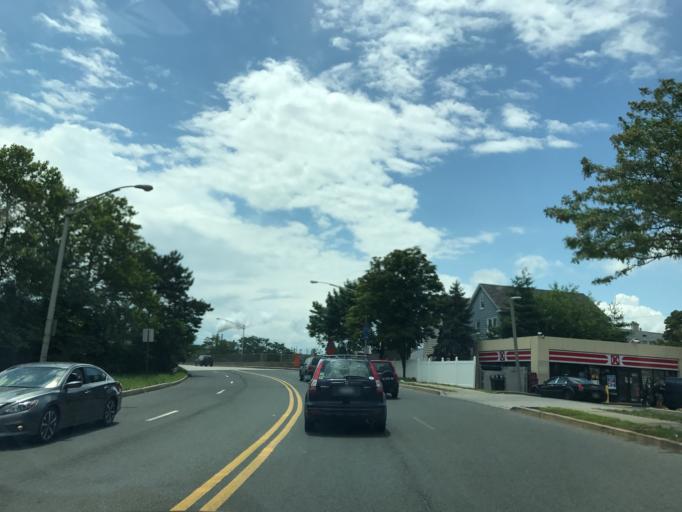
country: US
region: New Jersey
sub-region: Union County
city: Elizabeth
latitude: 40.6440
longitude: -74.2121
